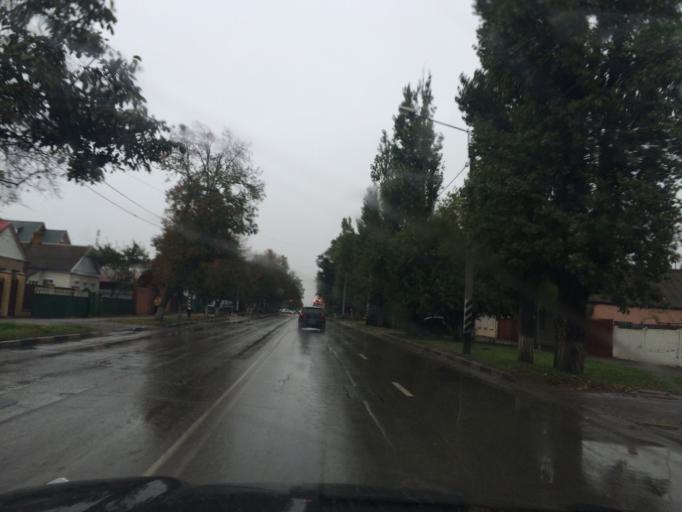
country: RU
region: Rostov
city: Azov
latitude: 47.0978
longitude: 39.4435
